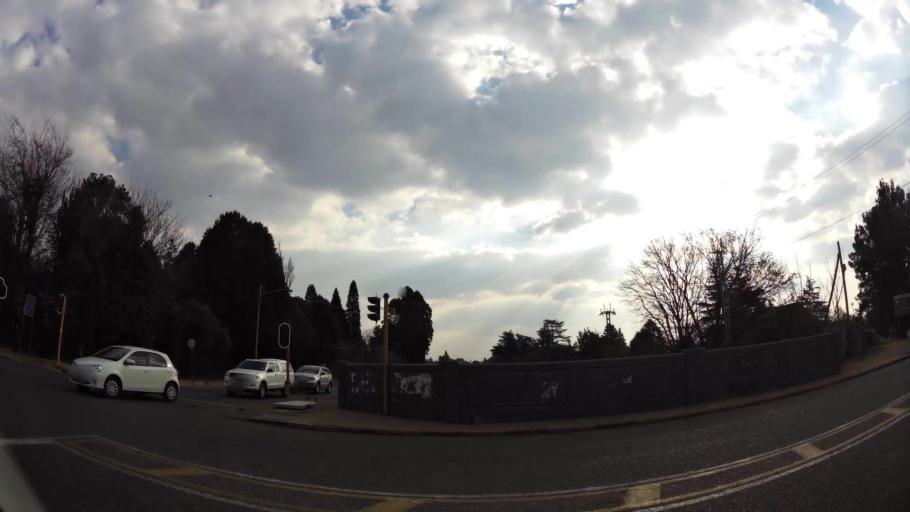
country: ZA
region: Gauteng
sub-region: Ekurhuleni Metropolitan Municipality
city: Germiston
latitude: -26.2334
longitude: 28.1738
